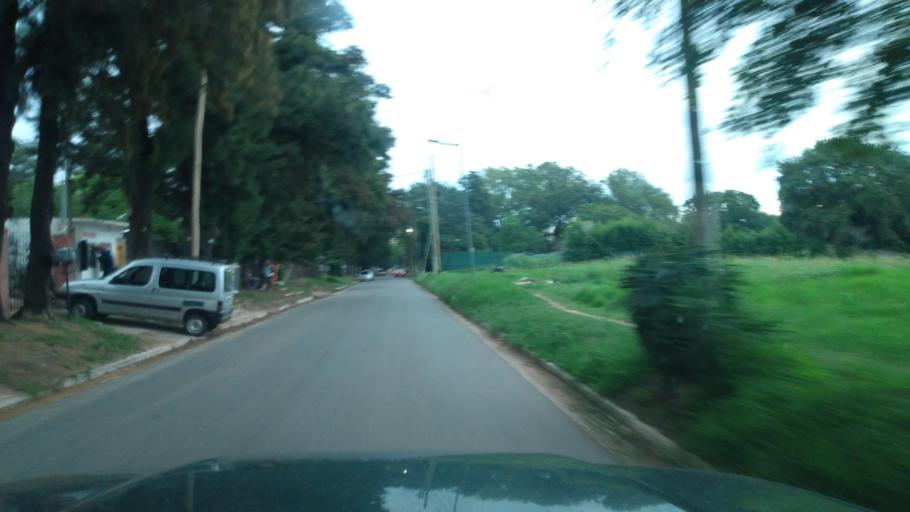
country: AR
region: Buenos Aires
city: Hurlingham
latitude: -34.5637
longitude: -58.7193
